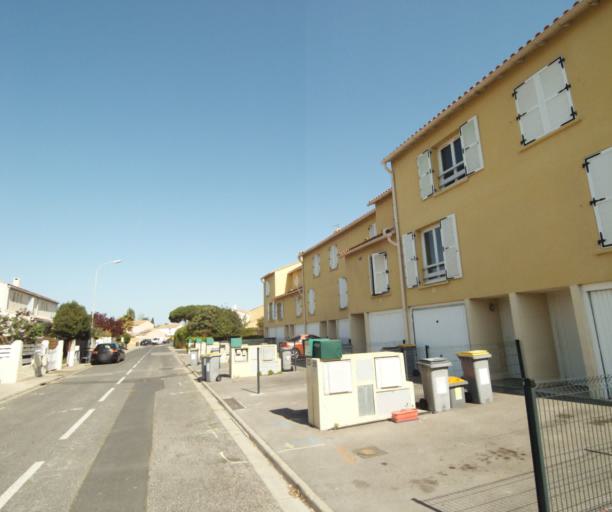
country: FR
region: Languedoc-Roussillon
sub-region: Departement de l'Herault
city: Lattes
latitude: 43.5735
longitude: 3.9135
